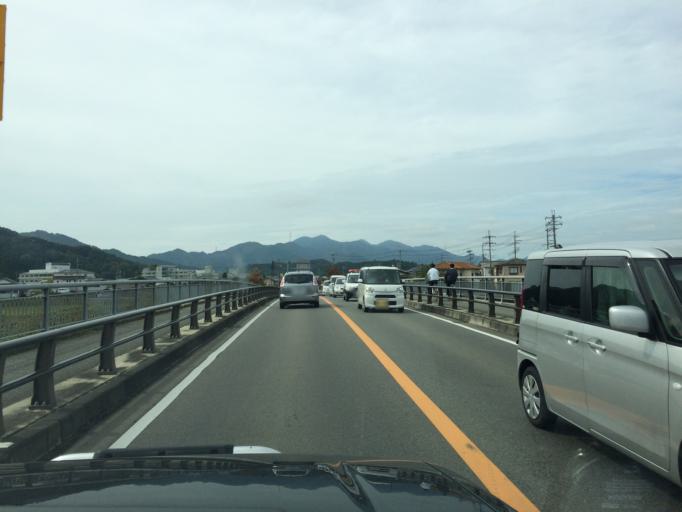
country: JP
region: Hyogo
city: Sasayama
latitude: 35.0741
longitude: 135.2024
